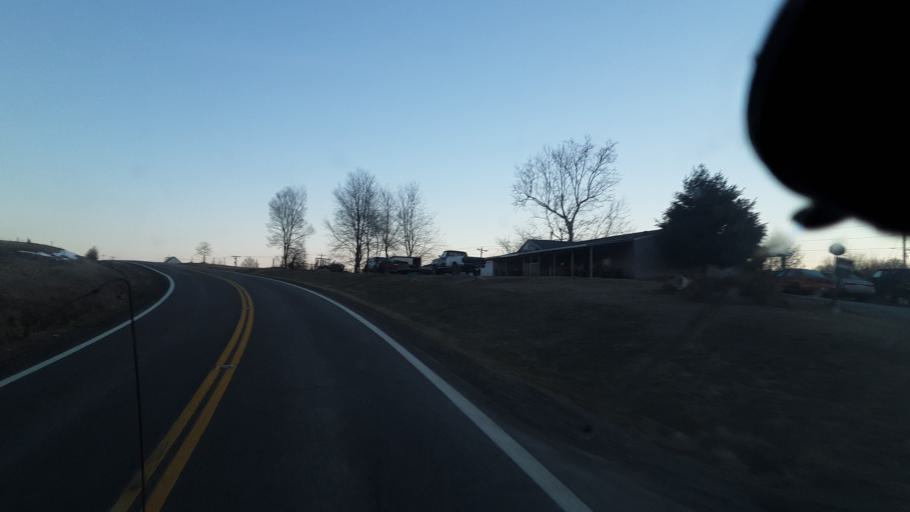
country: US
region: Ohio
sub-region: Perry County
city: Somerset
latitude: 39.7405
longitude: -82.3061
